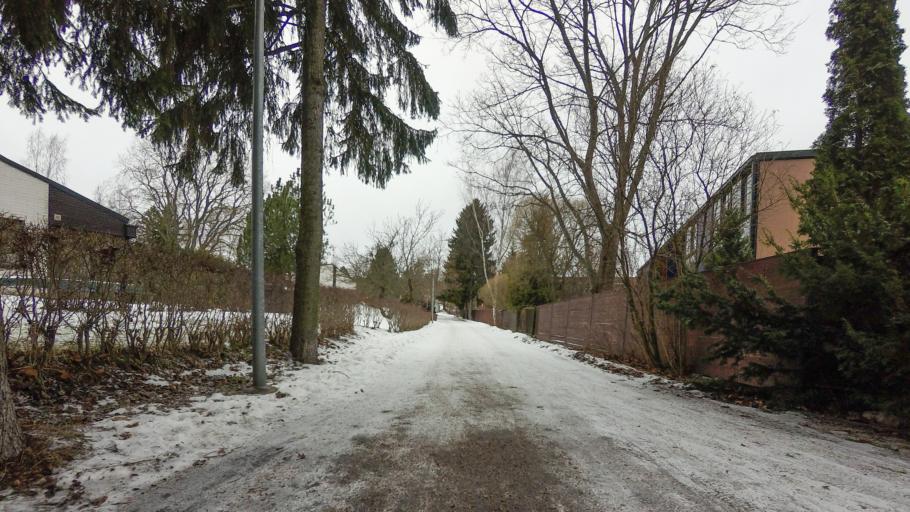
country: FI
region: Uusimaa
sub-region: Helsinki
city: Vantaa
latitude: 60.1898
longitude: 25.0608
